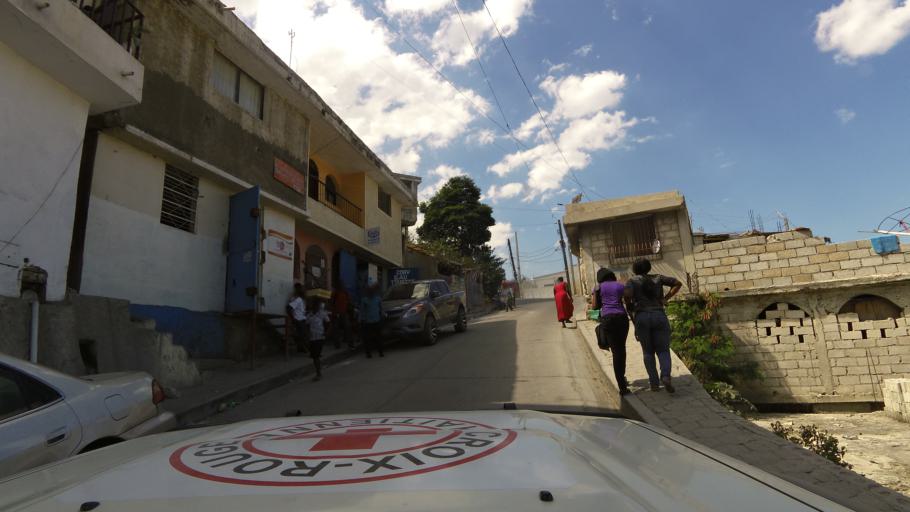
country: HT
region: Ouest
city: Petionville
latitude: 18.5285
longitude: -72.2921
